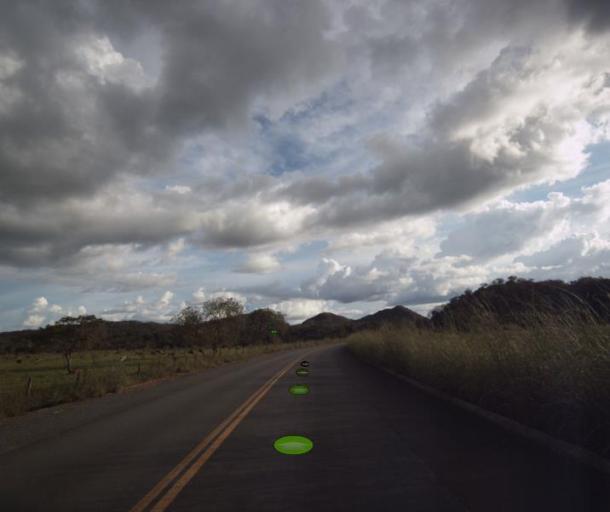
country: BR
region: Goias
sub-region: Niquelandia
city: Niquelandia
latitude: -14.5212
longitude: -48.5210
